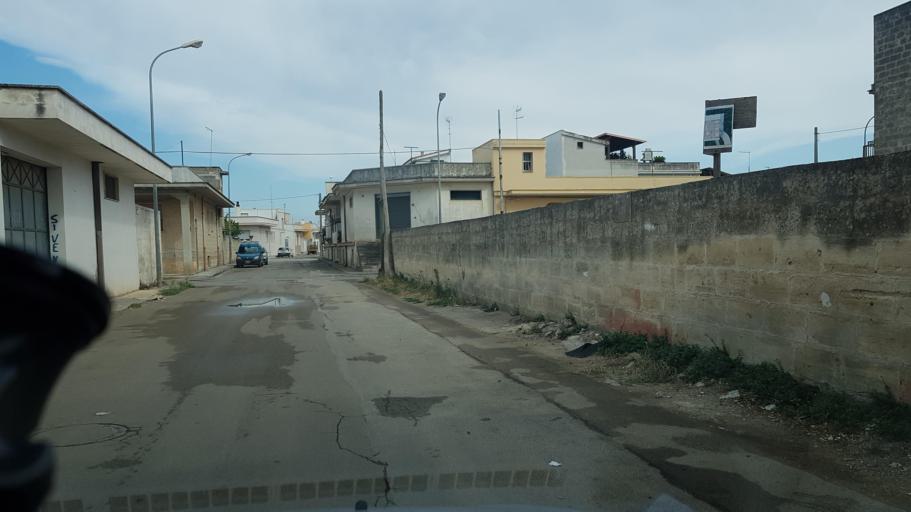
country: IT
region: Apulia
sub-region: Provincia di Brindisi
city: Torre Santa Susanna
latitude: 40.4742
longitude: 17.7402
